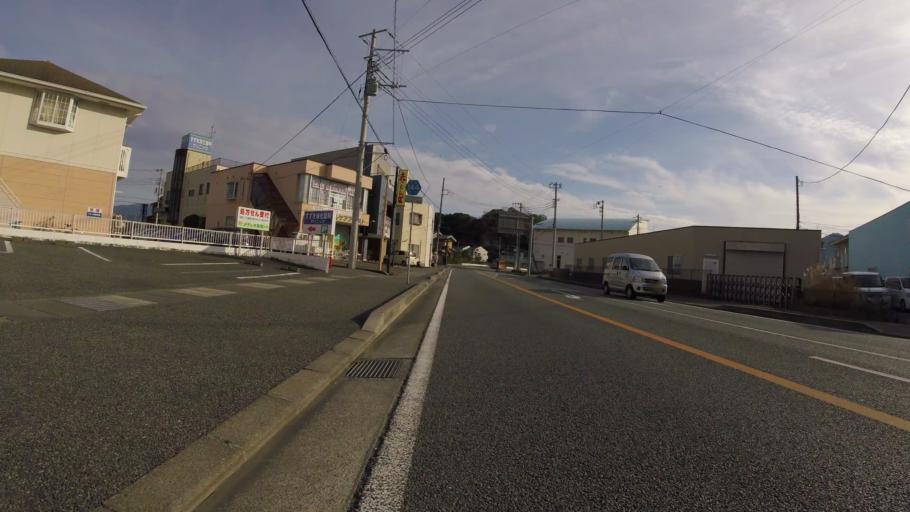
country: JP
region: Shizuoka
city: Mishima
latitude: 35.0891
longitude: 138.8982
